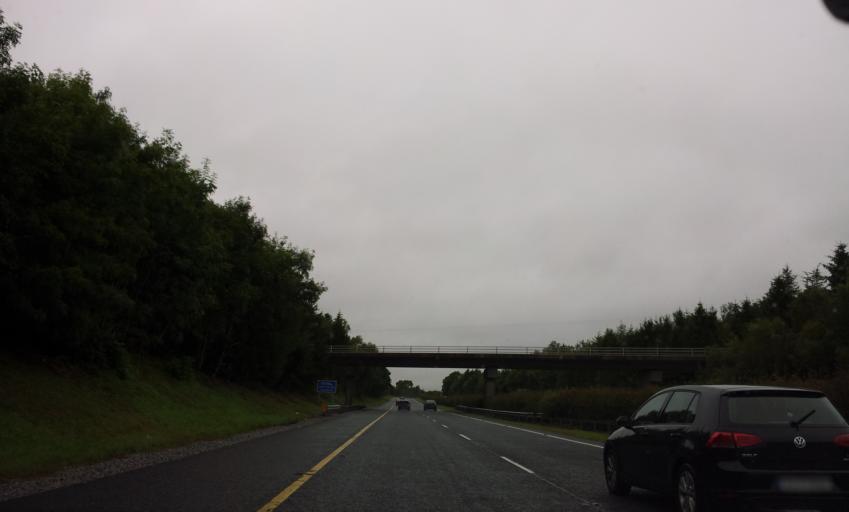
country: IE
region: Munster
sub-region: County Cork
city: Passage West
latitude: 51.9147
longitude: -8.3812
